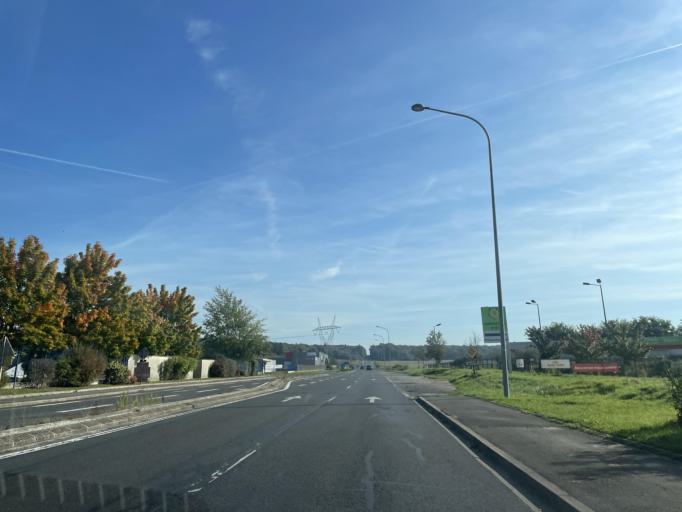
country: FR
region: Ile-de-France
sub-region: Departement de Seine-et-Marne
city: Trilport
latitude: 48.9581
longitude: 2.9592
